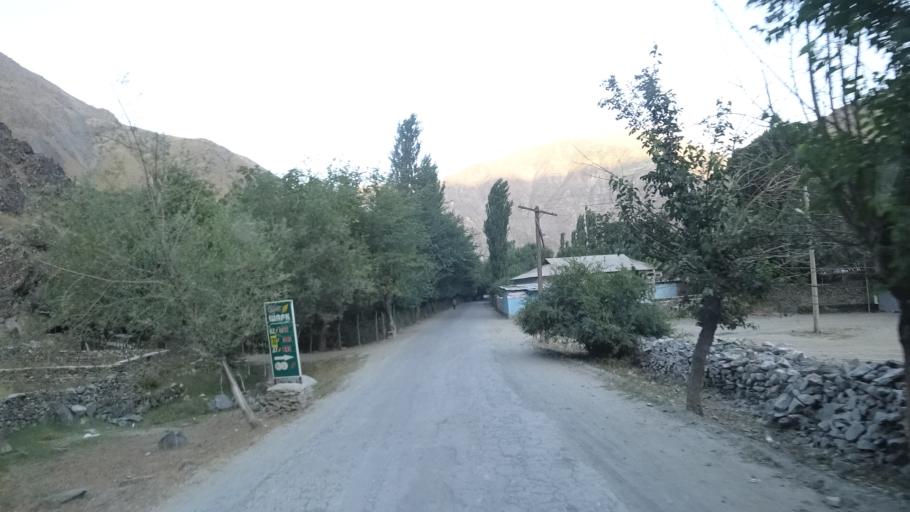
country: AF
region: Badakhshan
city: Nusay
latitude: 38.4550
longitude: 70.8276
